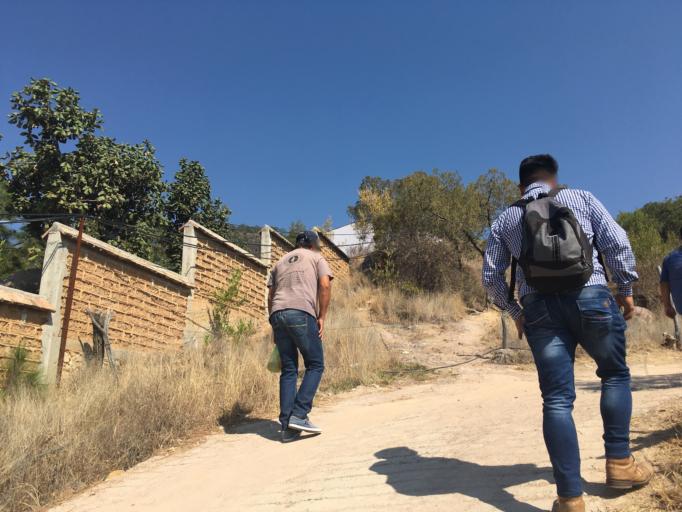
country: MX
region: Guerrero
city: Taxco de Alarcon
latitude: 18.5788
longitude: -99.6031
